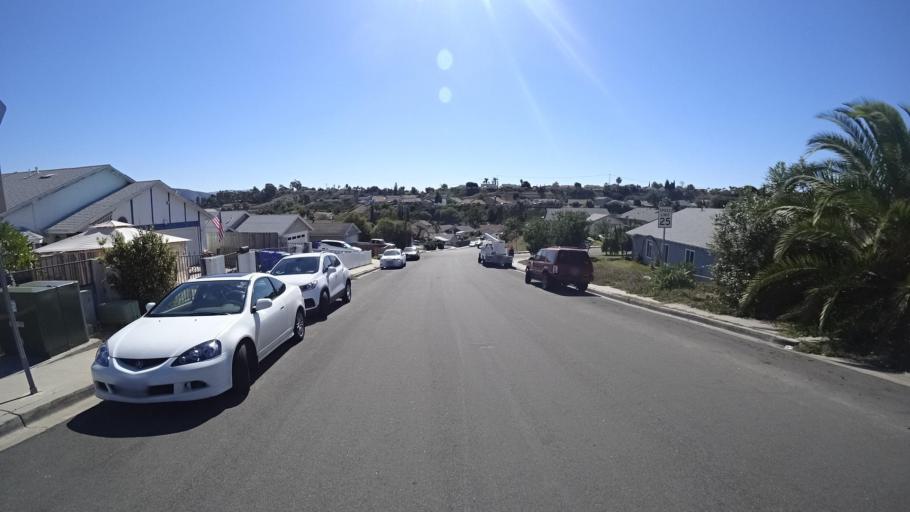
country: US
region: California
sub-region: San Diego County
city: La Presa
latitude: 32.7026
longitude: -117.0211
